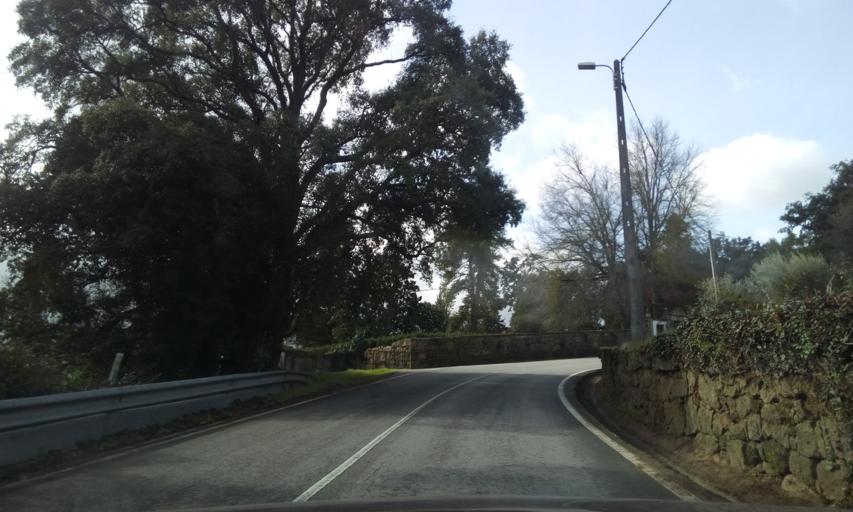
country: PT
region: Viseu
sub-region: Satao
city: Satao
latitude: 40.6711
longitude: -7.6964
